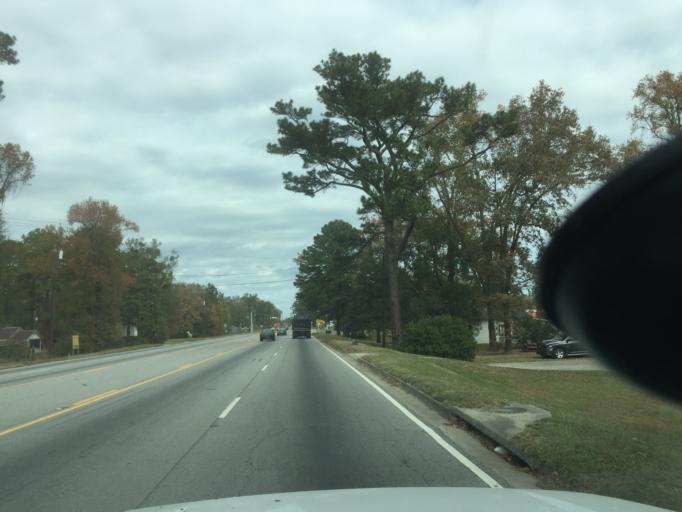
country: US
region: Georgia
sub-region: Chatham County
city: Garden City
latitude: 32.0941
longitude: -81.1965
